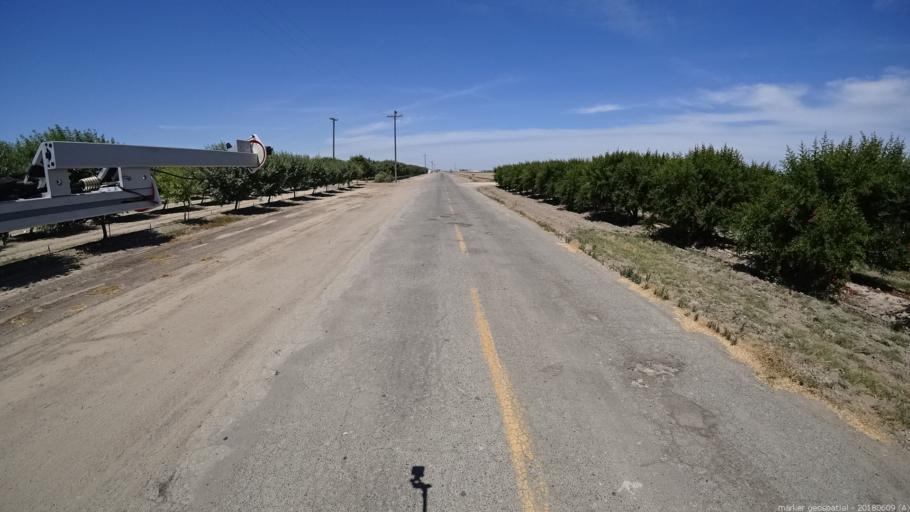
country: US
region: California
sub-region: Madera County
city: Fairmead
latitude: 36.9383
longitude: -120.2644
